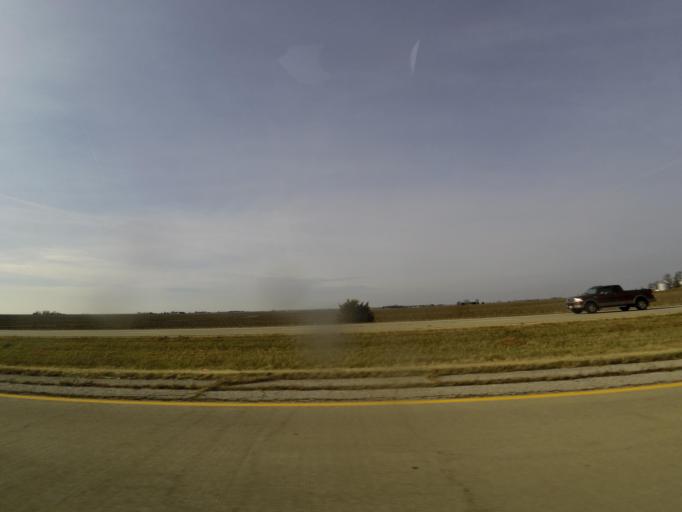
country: US
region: Illinois
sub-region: McLean County
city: Heyworth
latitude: 40.3827
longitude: -88.9891
